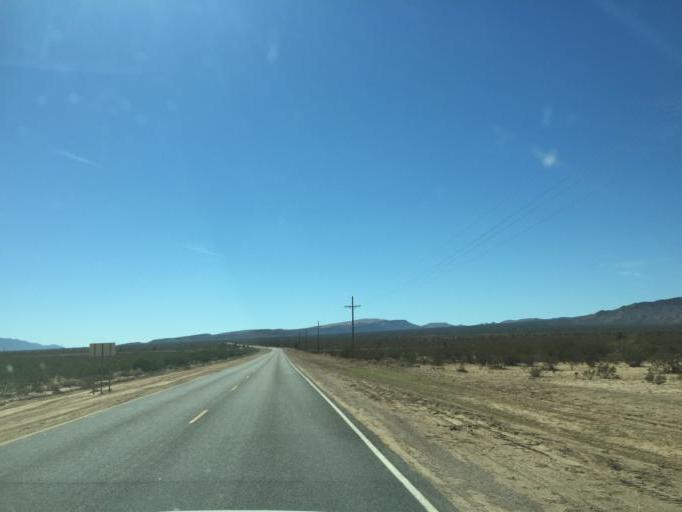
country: US
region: Arizona
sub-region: Mohave County
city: Meadview
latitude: 35.7813
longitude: -114.1288
